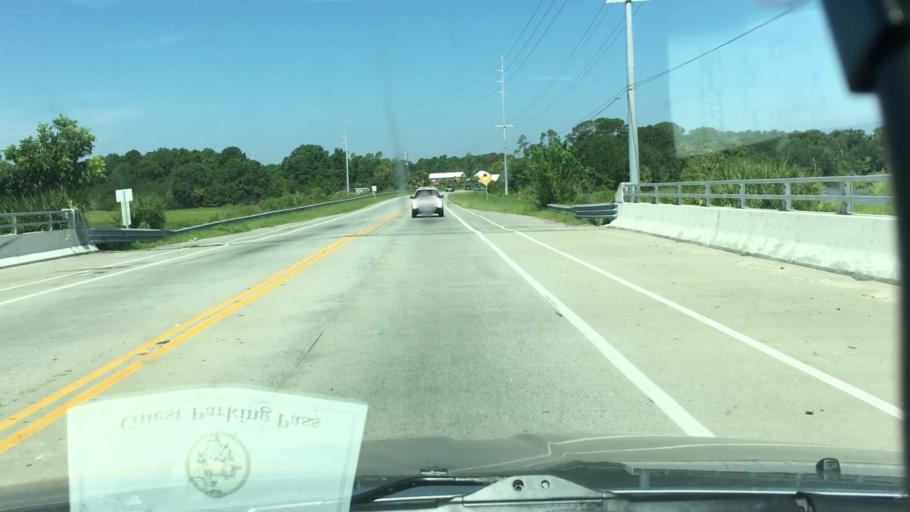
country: US
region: South Carolina
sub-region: Beaufort County
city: Beaufort
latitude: 32.3980
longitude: -80.6166
